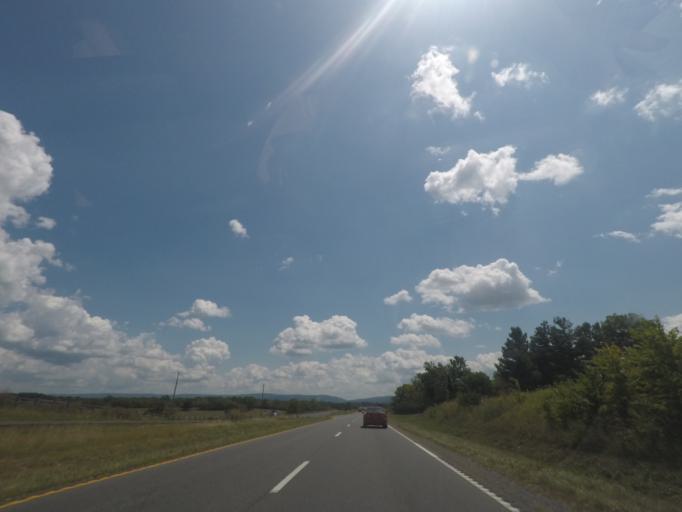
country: US
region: Virginia
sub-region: Warren County
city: Shenandoah Farms
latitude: 39.0884
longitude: -78.0930
